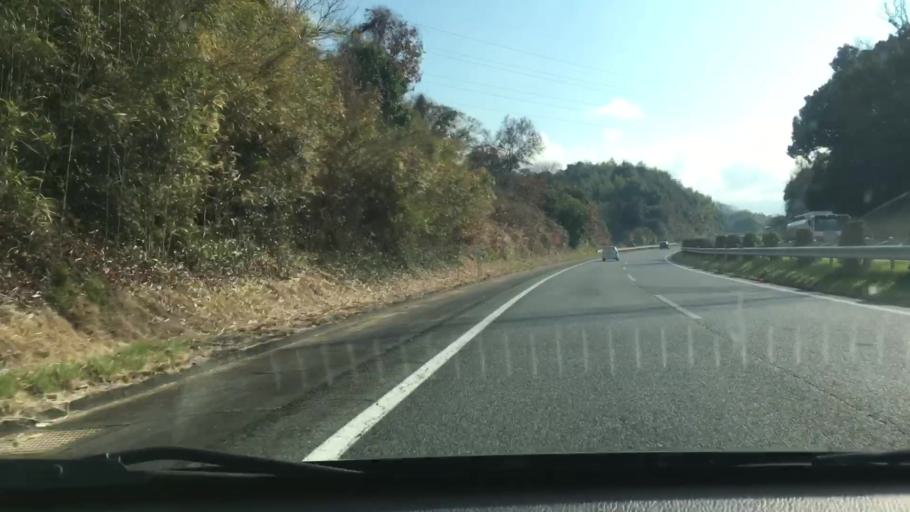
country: JP
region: Kumamoto
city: Matsubase
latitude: 32.6358
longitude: 130.7100
